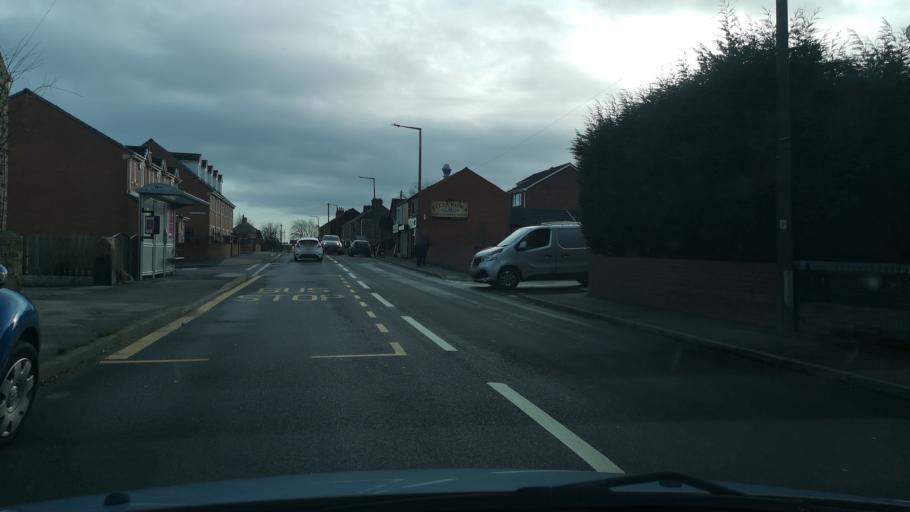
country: GB
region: England
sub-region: Barnsley
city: Great Houghton
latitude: 53.5556
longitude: -1.3534
